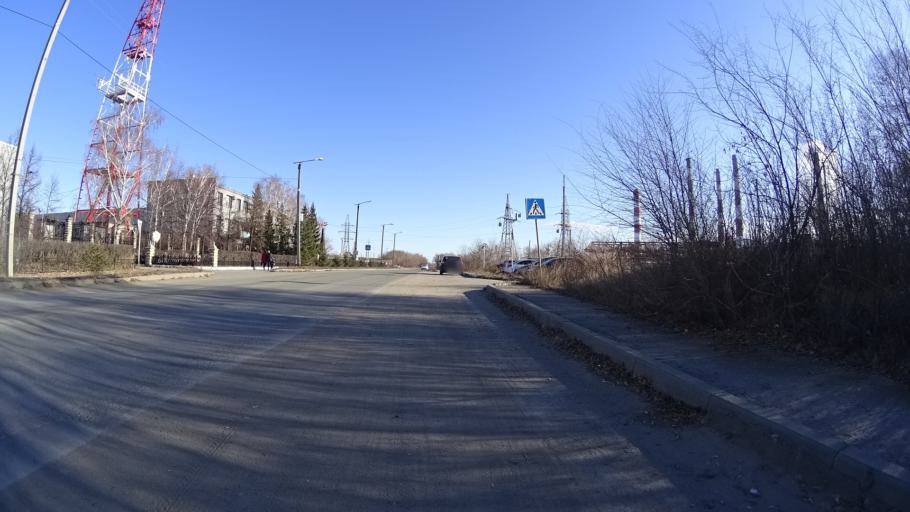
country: RU
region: Chelyabinsk
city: Troitsk
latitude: 54.0414
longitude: 61.6396
